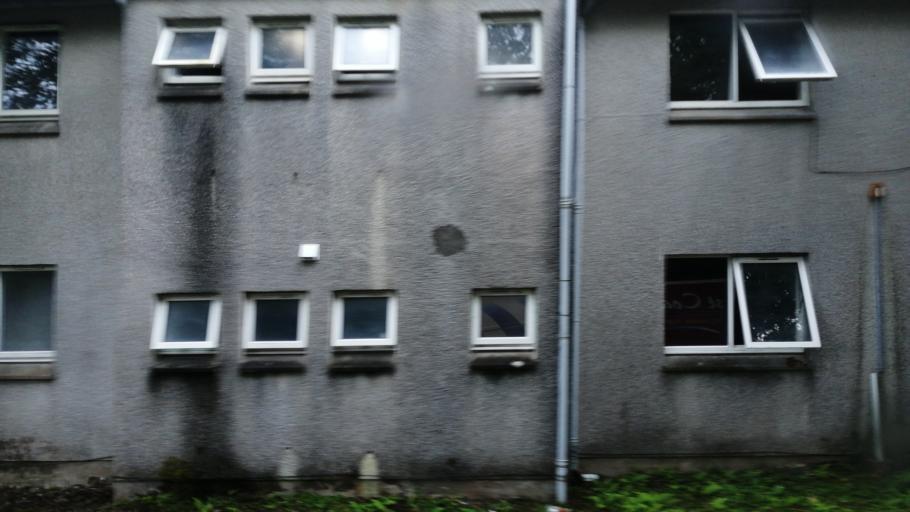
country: GB
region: Scotland
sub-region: Argyll and Bute
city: Isle Of Mull
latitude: 56.4776
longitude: -5.7153
